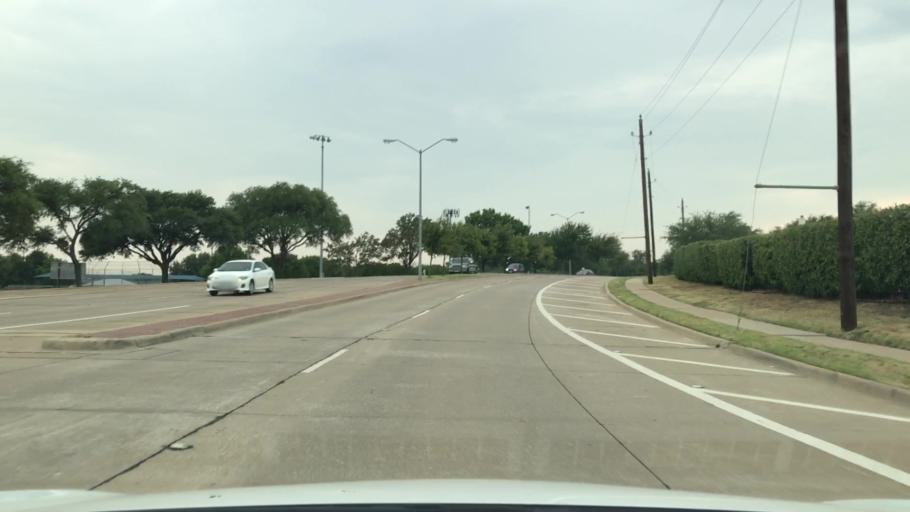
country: US
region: Texas
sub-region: Dallas County
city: Carrollton
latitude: 32.9687
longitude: -96.8967
